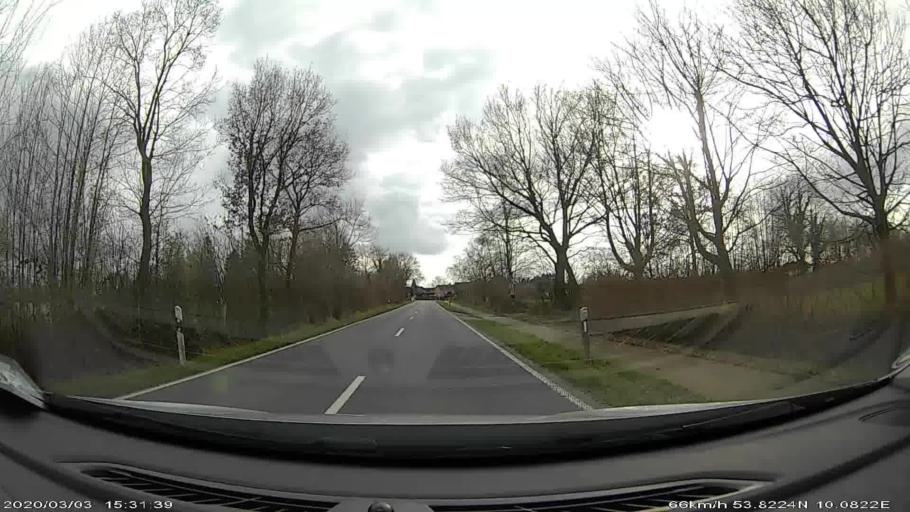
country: DE
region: Schleswig-Holstein
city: Huttblek
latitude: 53.8233
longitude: 10.0827
